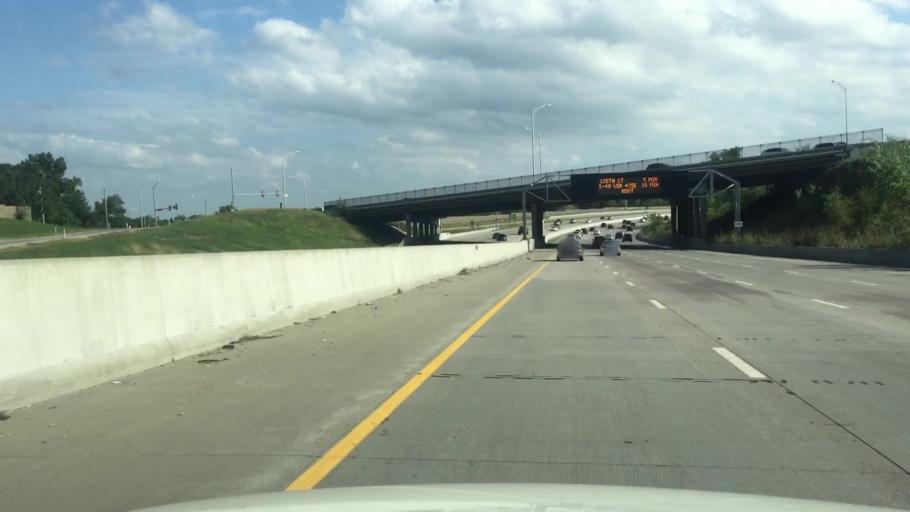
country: US
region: Kansas
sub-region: Johnson County
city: Lenexa
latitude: 38.9577
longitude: -94.7092
